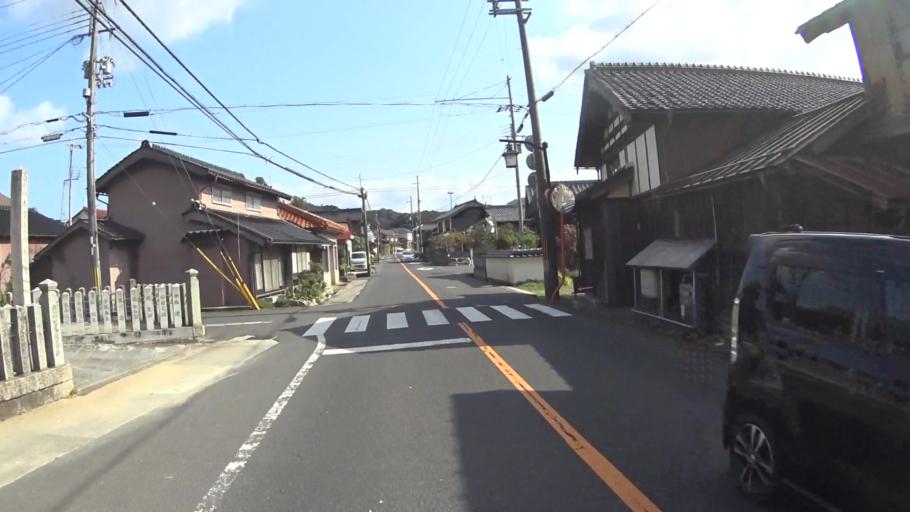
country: JP
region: Kyoto
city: Miyazu
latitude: 35.5897
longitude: 135.1010
